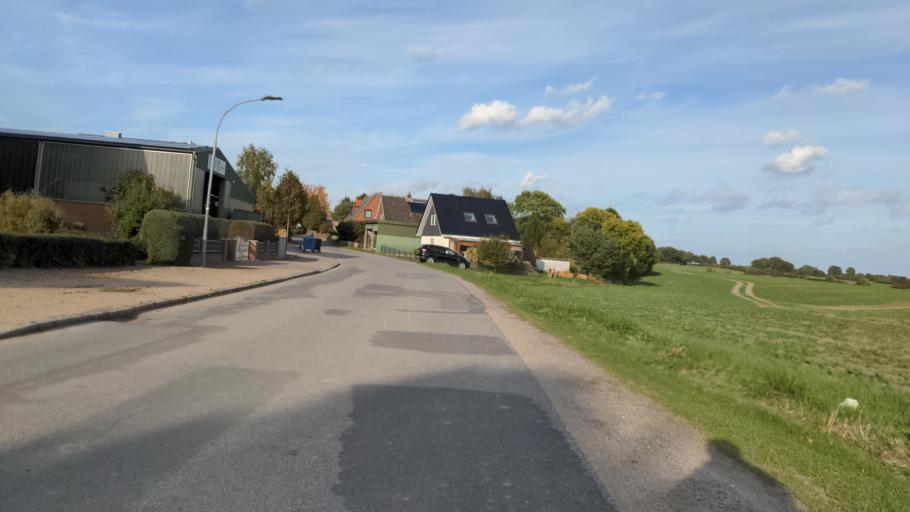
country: DE
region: Schleswig-Holstein
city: Ahrensbok
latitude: 53.9633
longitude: 10.5320
